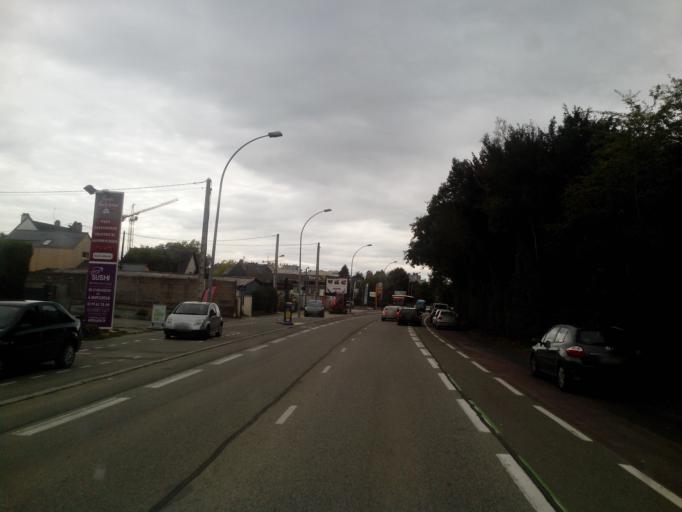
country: FR
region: Brittany
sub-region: Departement d'Ille-et-Vilaine
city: Rennes
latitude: 48.1287
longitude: -1.6476
